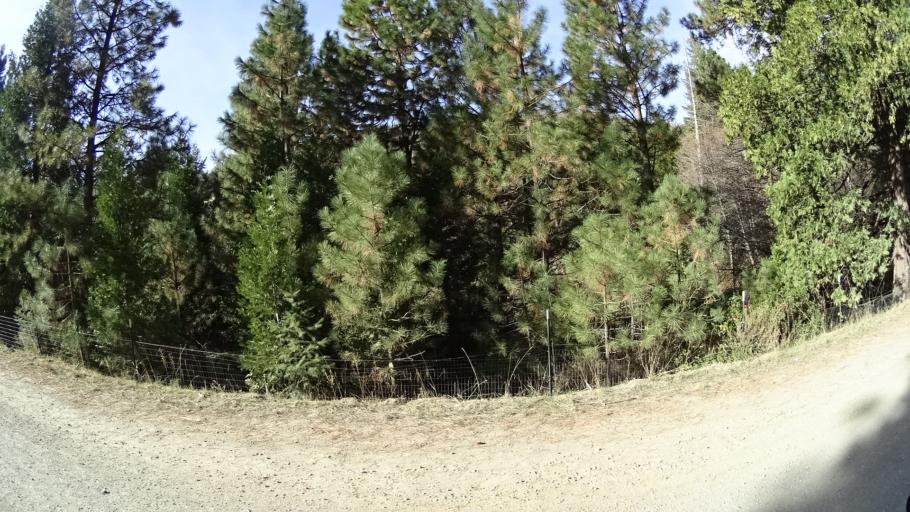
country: US
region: California
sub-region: Siskiyou County
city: Weed
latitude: 41.4358
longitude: -122.4237
